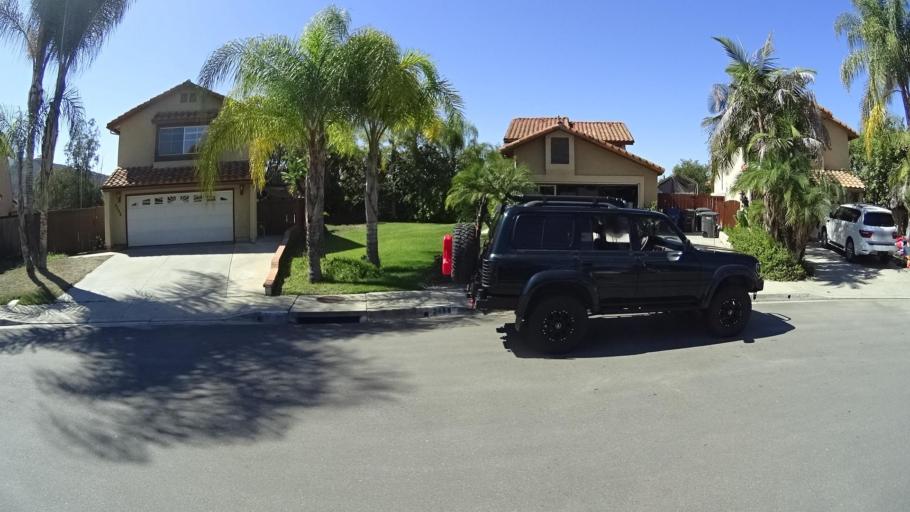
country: US
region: California
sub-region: San Diego County
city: Rancho San Diego
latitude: 32.7439
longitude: -116.9262
